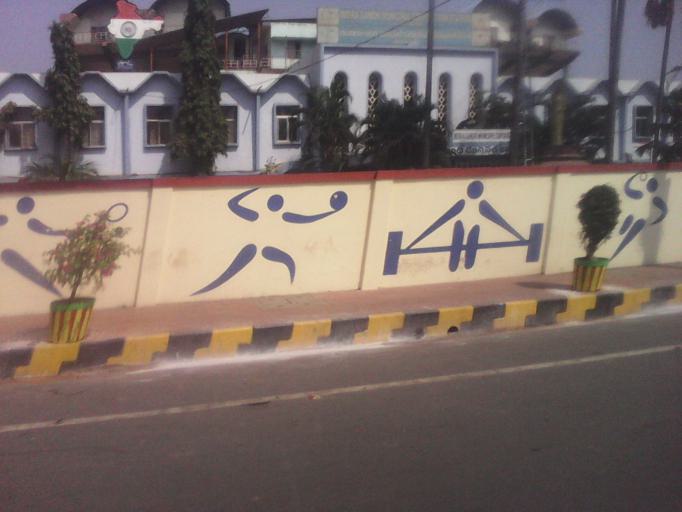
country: IN
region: Andhra Pradesh
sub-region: Krishna
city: Vijayawada
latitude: 16.5038
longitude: 80.6374
